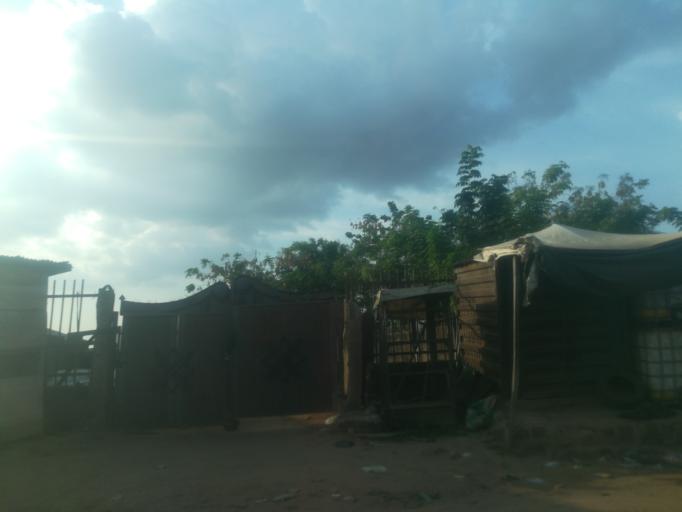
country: NG
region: Ogun
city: Abeokuta
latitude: 7.1279
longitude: 3.3259
